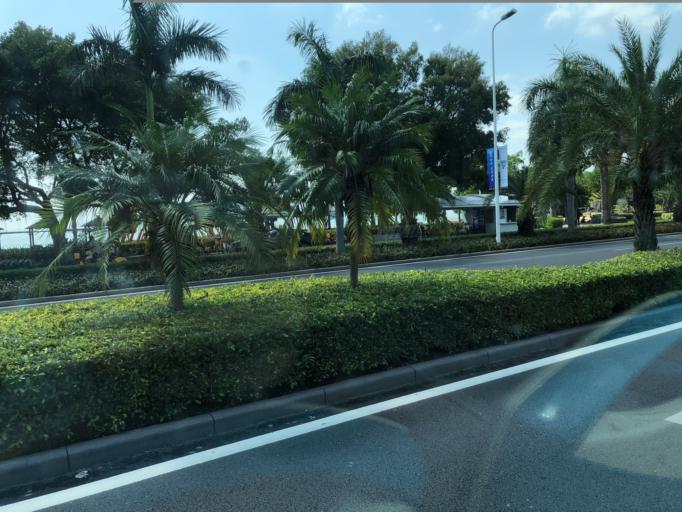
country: CN
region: Fujian
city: Xiamen
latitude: 24.4269
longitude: 118.1239
